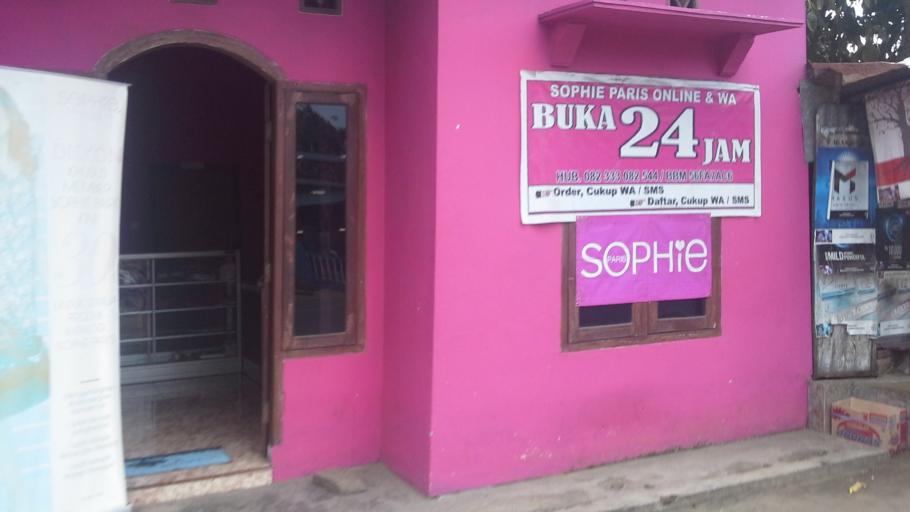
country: ID
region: East Java
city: Bondowoso
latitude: -7.9133
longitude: 113.8436
